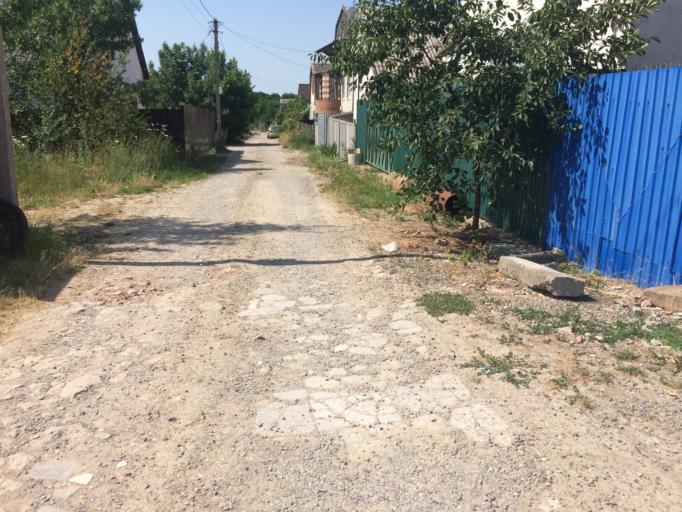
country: RU
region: Stavropol'skiy
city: Tatarka
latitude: 44.9819
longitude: 41.9410
